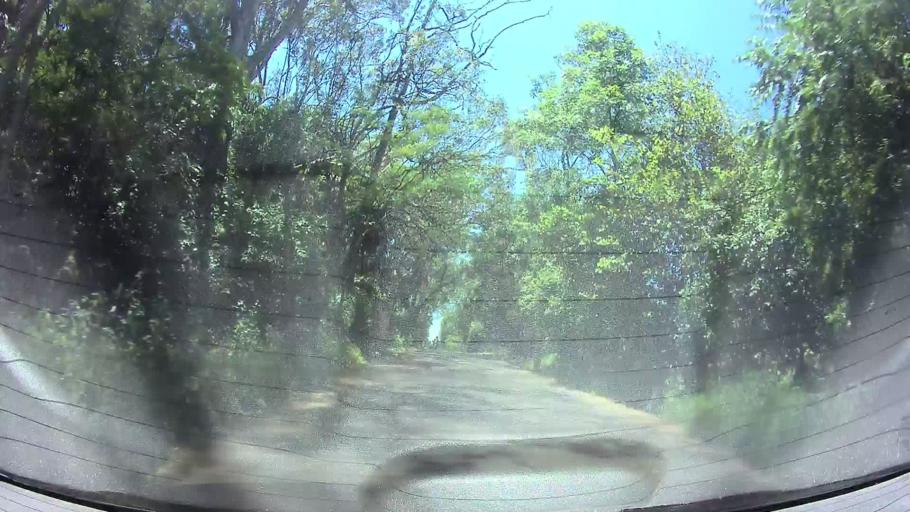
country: PY
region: Central
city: Fernando de la Mora
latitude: -25.2712
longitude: -57.5160
